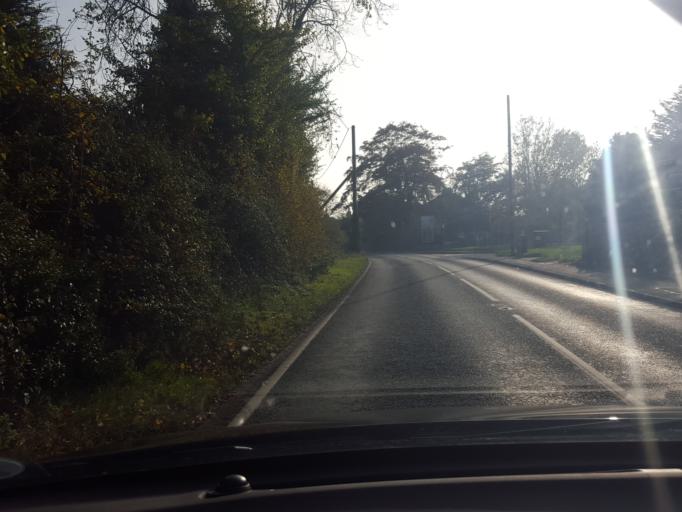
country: GB
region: England
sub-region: Essex
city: Dovercourt
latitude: 51.9229
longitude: 1.2307
